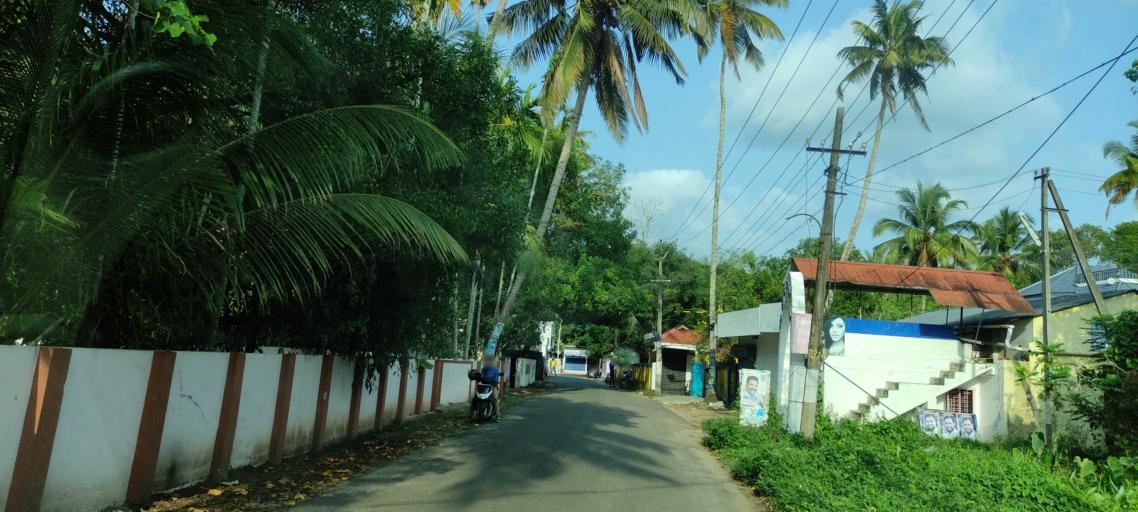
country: IN
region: Kerala
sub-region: Alappuzha
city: Vayalar
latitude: 9.7282
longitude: 76.2981
